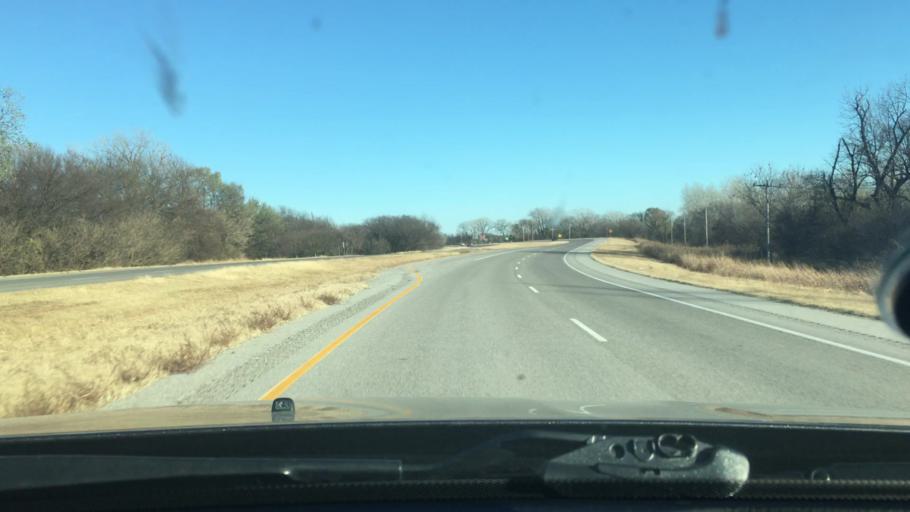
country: US
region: Oklahoma
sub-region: Murray County
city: Davis
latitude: 34.5061
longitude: -97.1489
